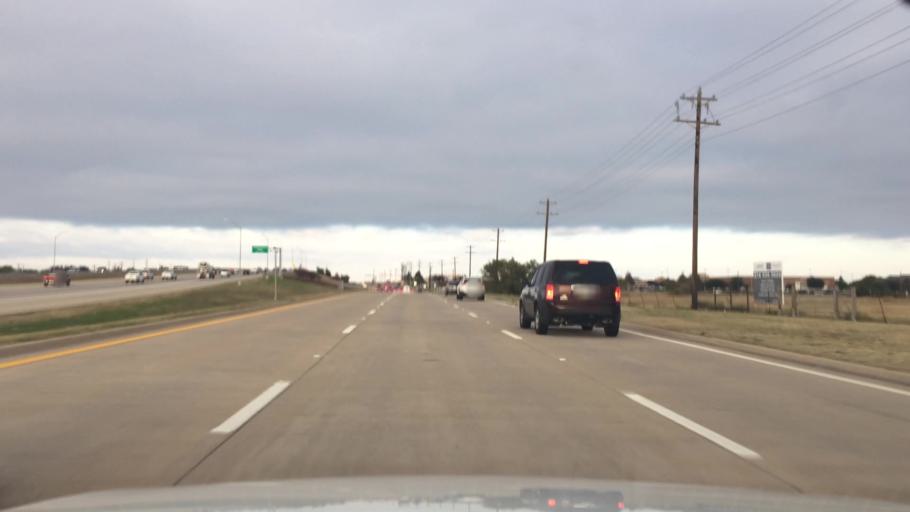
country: US
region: Texas
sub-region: Collin County
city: Frisco
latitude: 33.1096
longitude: -96.7733
